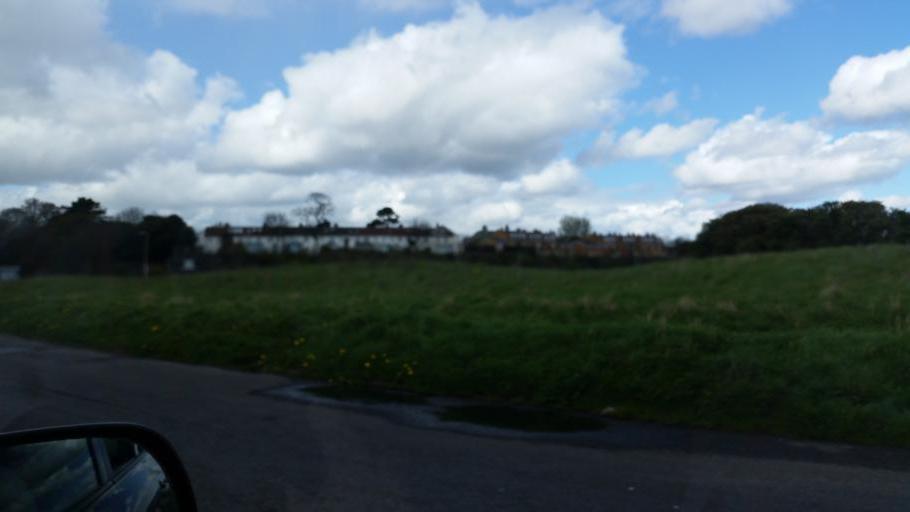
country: IE
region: Leinster
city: Dollymount
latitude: 53.3733
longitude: -6.1629
